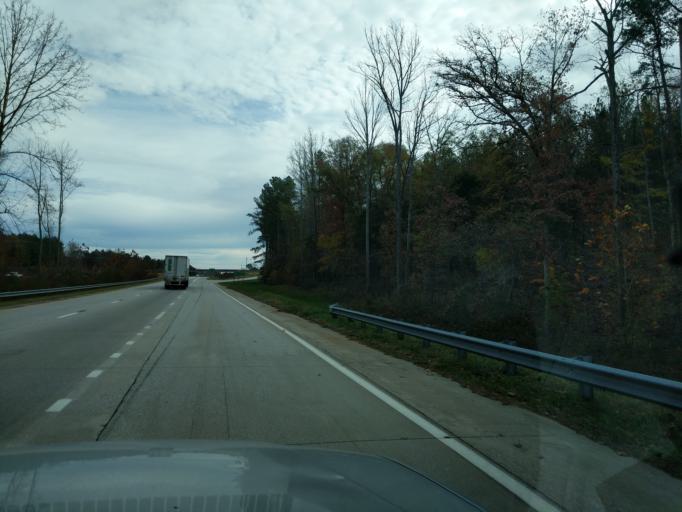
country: US
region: South Carolina
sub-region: Laurens County
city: Watts Mills
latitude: 34.5398
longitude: -81.9608
